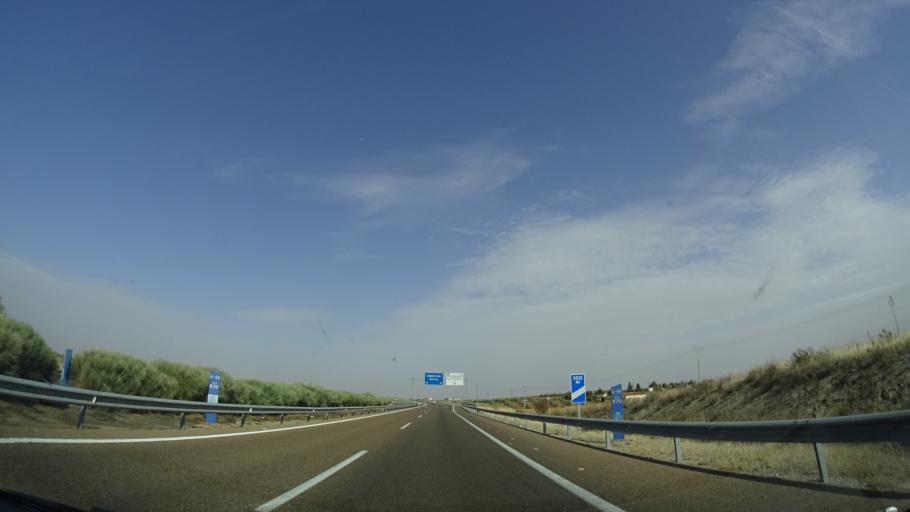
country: ES
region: Extremadura
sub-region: Provincia de Badajoz
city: Villafranca de los Barros
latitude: 38.5194
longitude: -6.3501
